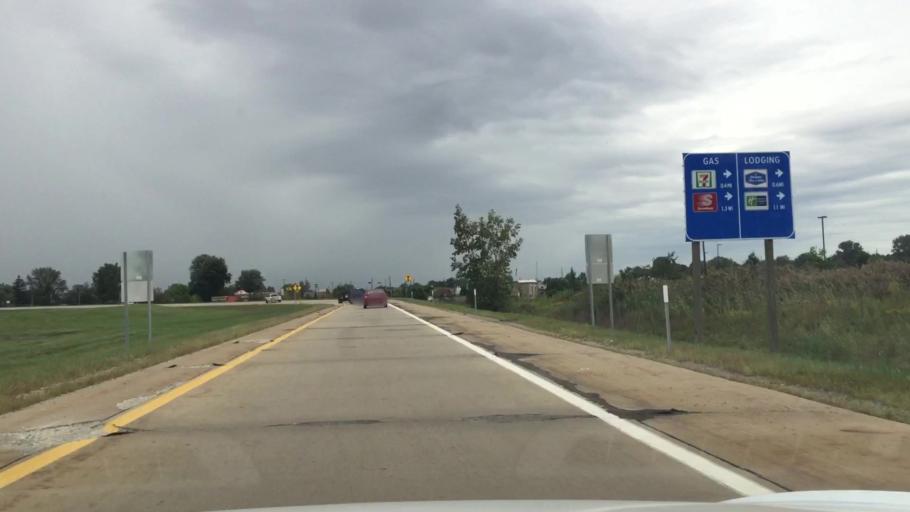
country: US
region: Michigan
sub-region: Macomb County
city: Mount Clemens
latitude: 42.6330
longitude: -82.8494
